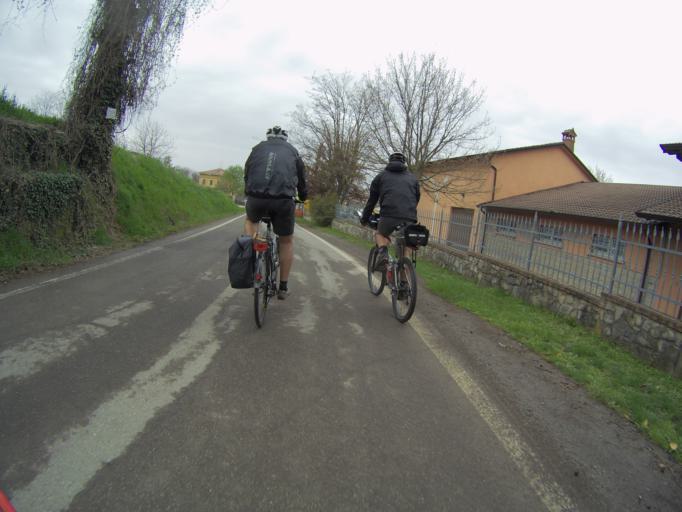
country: IT
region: Emilia-Romagna
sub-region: Provincia di Reggio Emilia
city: Ciano d'Enza
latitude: 44.5916
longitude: 10.4545
